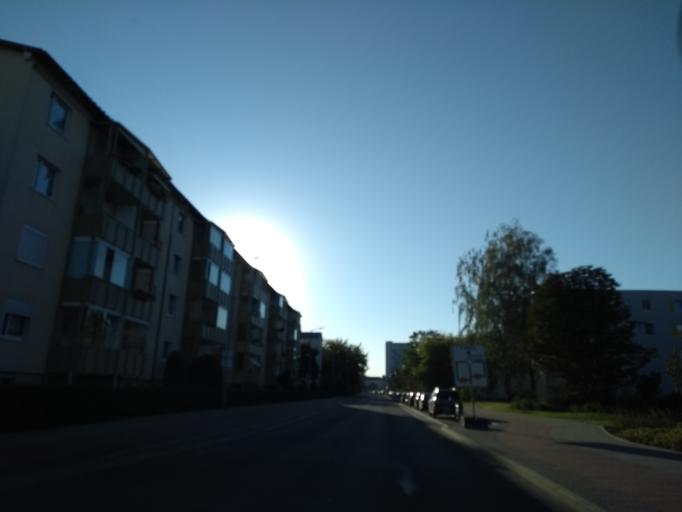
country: DE
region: Brandenburg
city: Lubbenau
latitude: 51.8602
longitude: 13.9451
